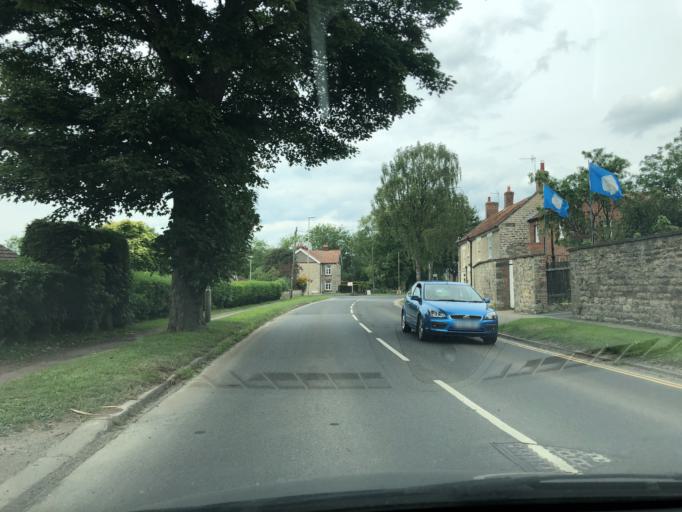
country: GB
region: England
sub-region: North Yorkshire
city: Pickering
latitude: 54.2490
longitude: -0.7914
